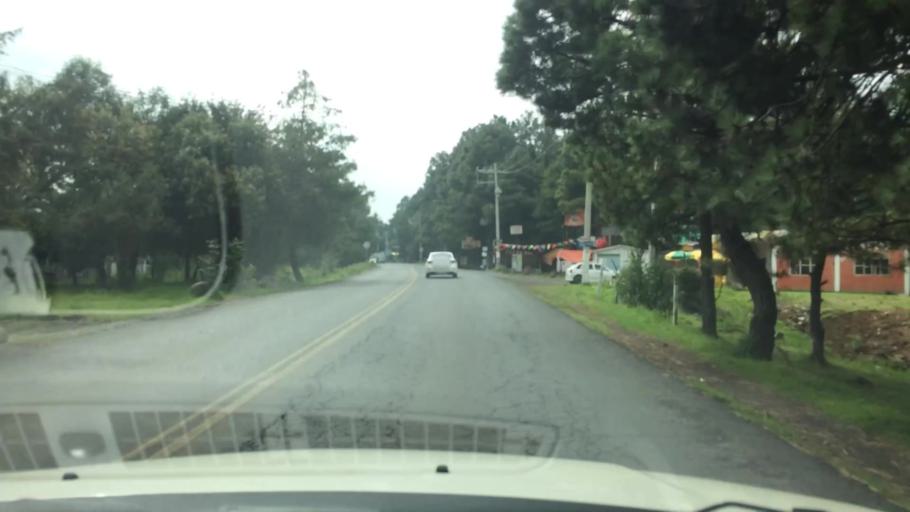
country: MX
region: Mexico City
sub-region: Tlalpan
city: Lomas de Tepemecatl
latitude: 19.2449
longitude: -99.2413
